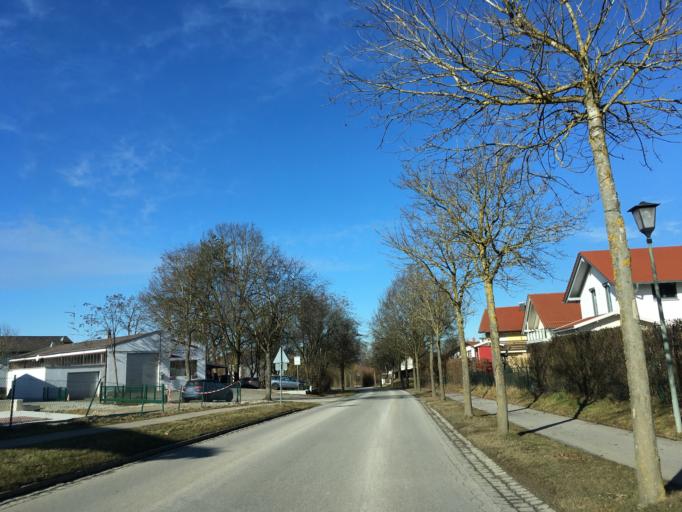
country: DE
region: Bavaria
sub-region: Upper Bavaria
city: Obertaufkirchen
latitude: 48.2603
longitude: 12.2814
